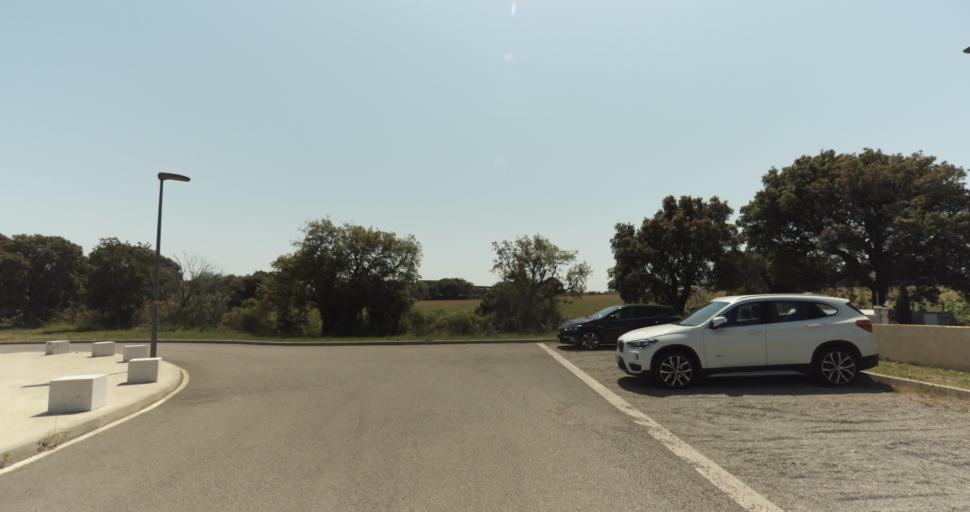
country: FR
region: Corsica
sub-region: Departement de la Haute-Corse
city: Biguglia
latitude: 42.5996
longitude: 9.4336
